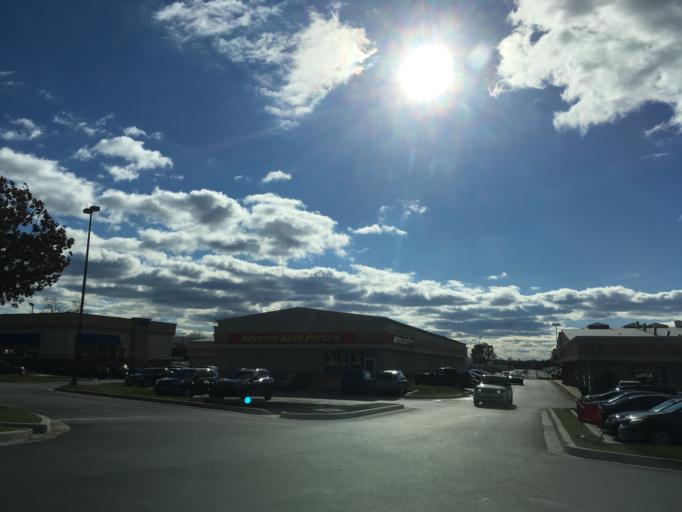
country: US
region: Maryland
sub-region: Anne Arundel County
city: Jessup
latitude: 39.1697
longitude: -76.7845
